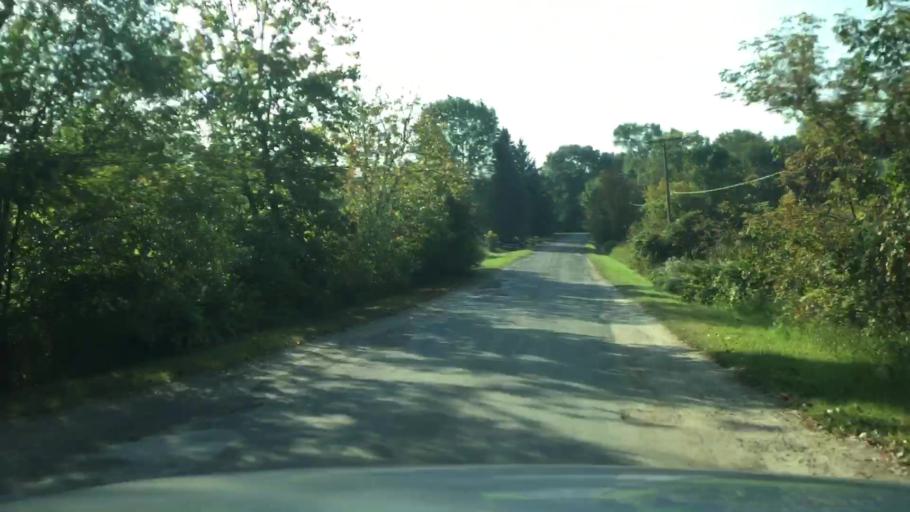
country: US
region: Michigan
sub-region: Livingston County
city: Whitmore Lake
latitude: 42.4436
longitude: -83.8327
